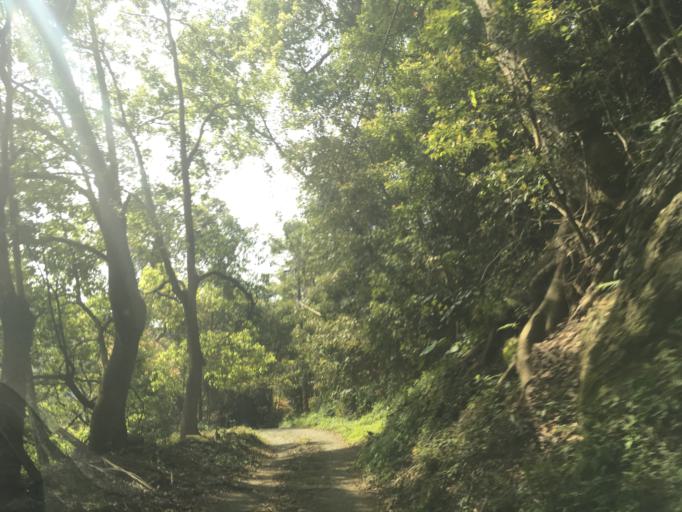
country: TW
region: Taiwan
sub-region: Taichung City
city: Taichung
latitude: 24.1351
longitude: 120.8210
